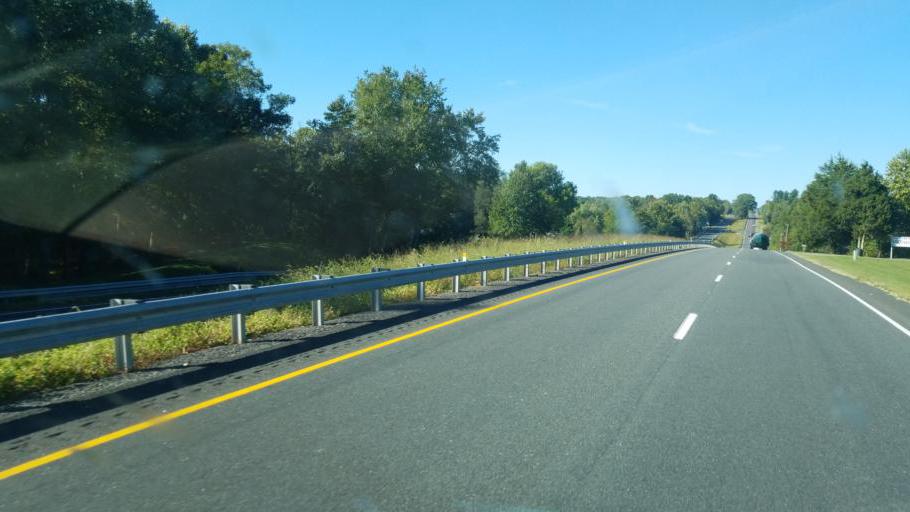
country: US
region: Virginia
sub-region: Madison County
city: Brightwood
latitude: 38.4338
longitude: -78.1584
